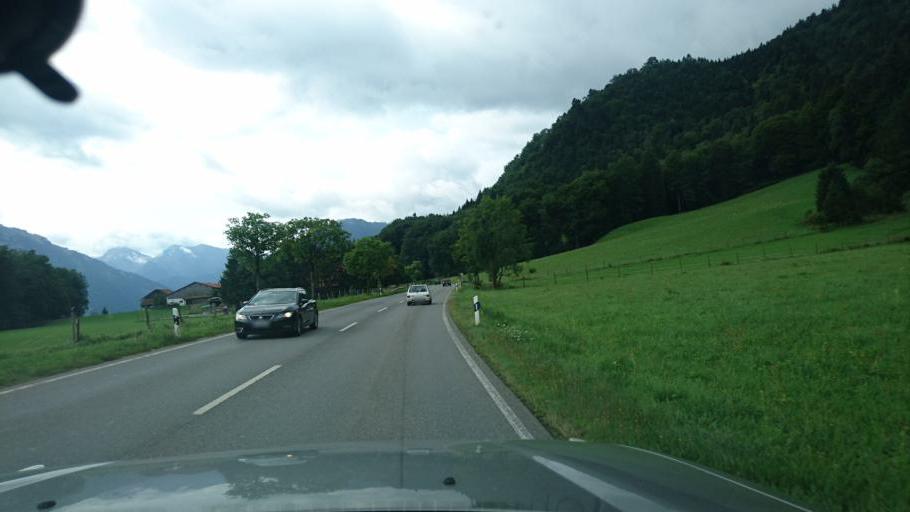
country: DE
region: Bavaria
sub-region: Upper Bavaria
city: Ruhpolding
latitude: 47.7773
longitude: 12.6383
